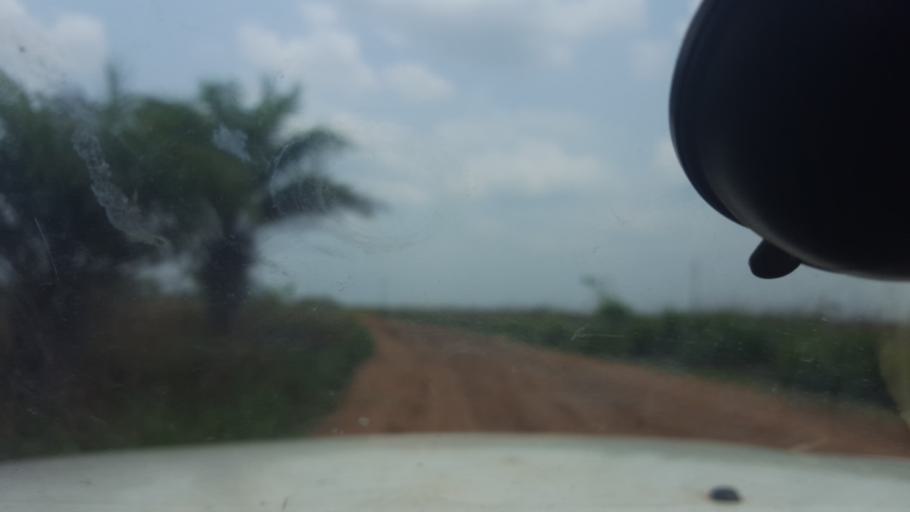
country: CD
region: Bandundu
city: Bandundu
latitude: -3.3318
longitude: 17.2862
